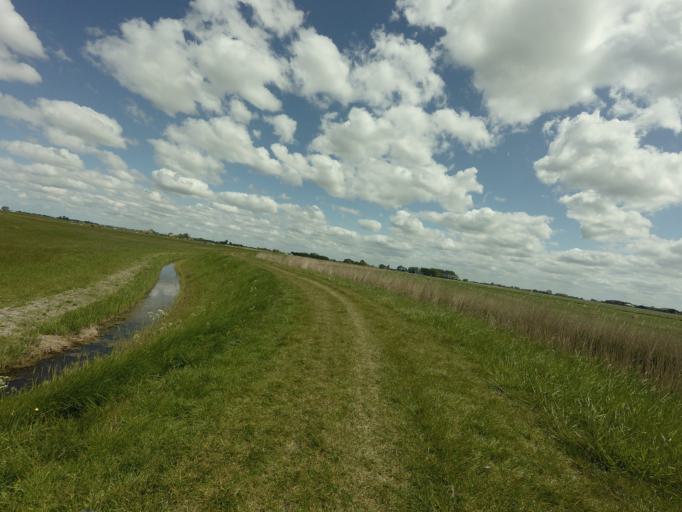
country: NL
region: Friesland
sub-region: Gemeente Franekeradeel
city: Franeker
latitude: 53.1452
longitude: 5.5078
